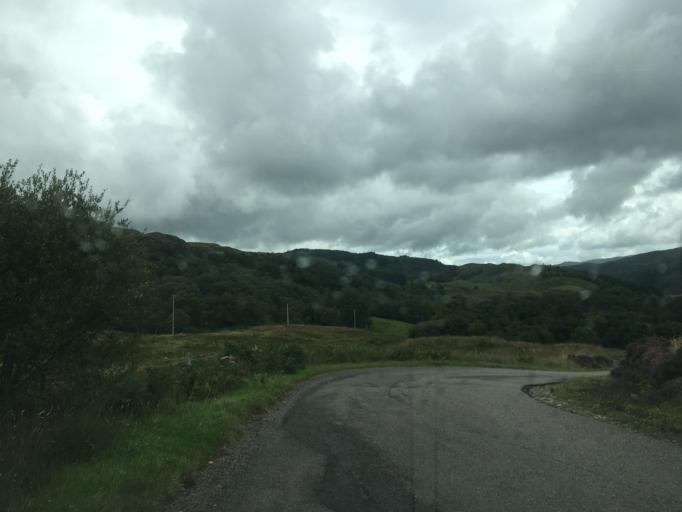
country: GB
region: Scotland
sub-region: Argyll and Bute
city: Oban
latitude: 56.2859
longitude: -5.3290
